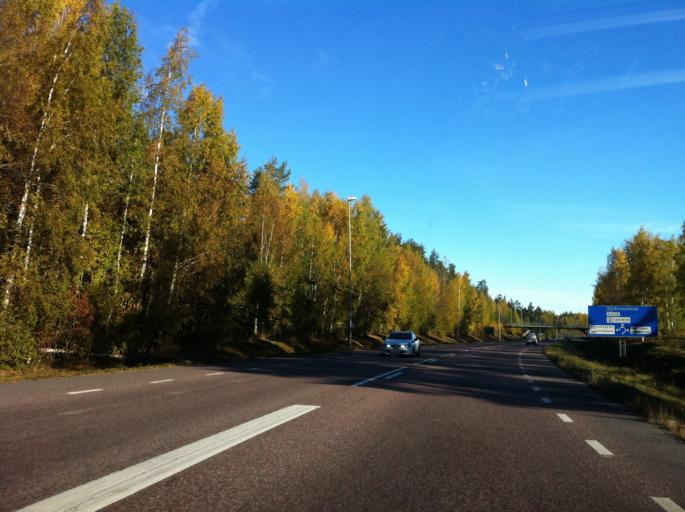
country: SE
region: Gaevleborg
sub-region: Gavle Kommun
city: Gavle
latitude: 60.6449
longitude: 17.1430
